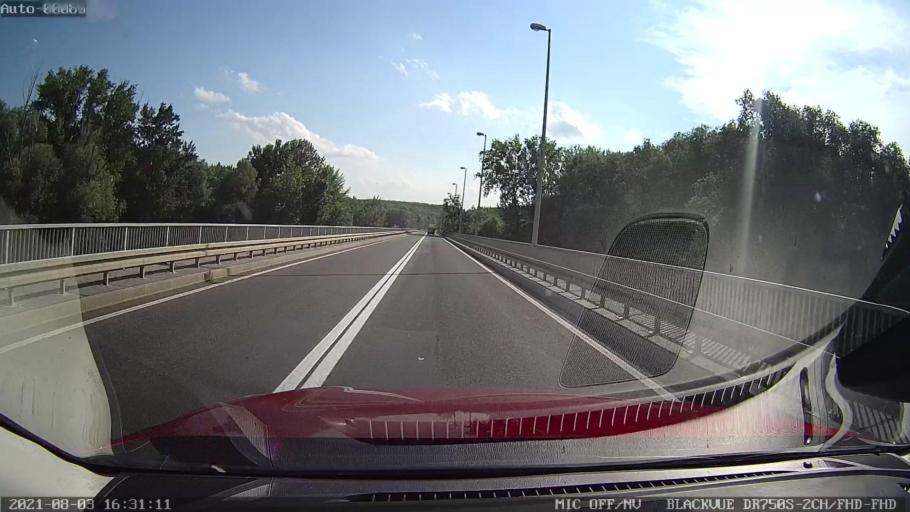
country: HR
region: Osjecko-Baranjska
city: Visnjevac
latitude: 45.5753
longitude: 18.6387
